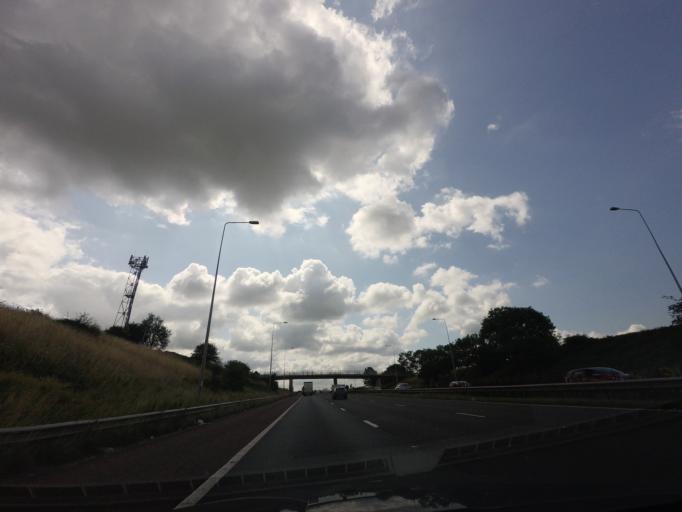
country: GB
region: England
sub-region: Lancashire
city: Euxton
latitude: 53.6443
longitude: -2.6922
